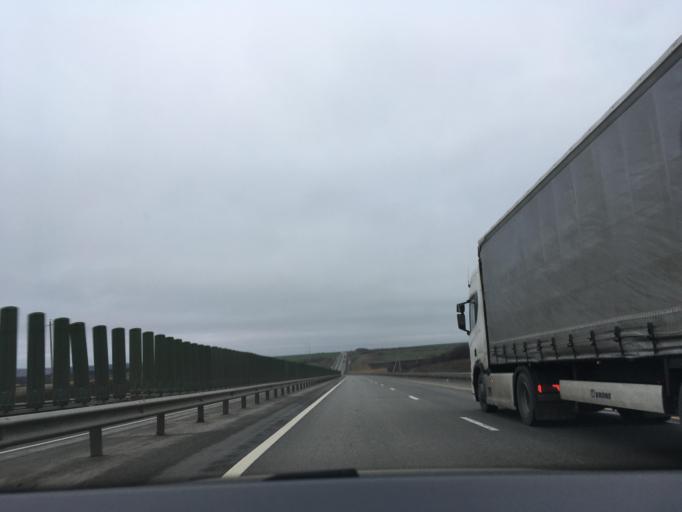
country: RU
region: Rostov
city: Glubokiy
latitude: 48.5982
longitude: 40.3538
